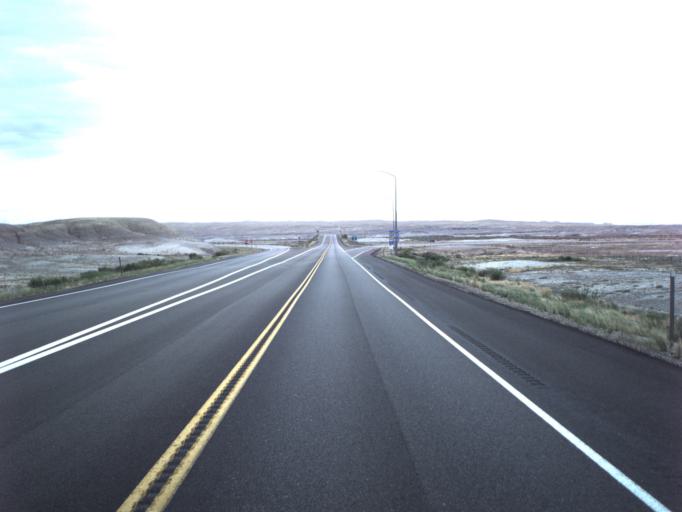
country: US
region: Utah
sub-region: Carbon County
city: East Carbon City
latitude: 38.9859
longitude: -110.2402
